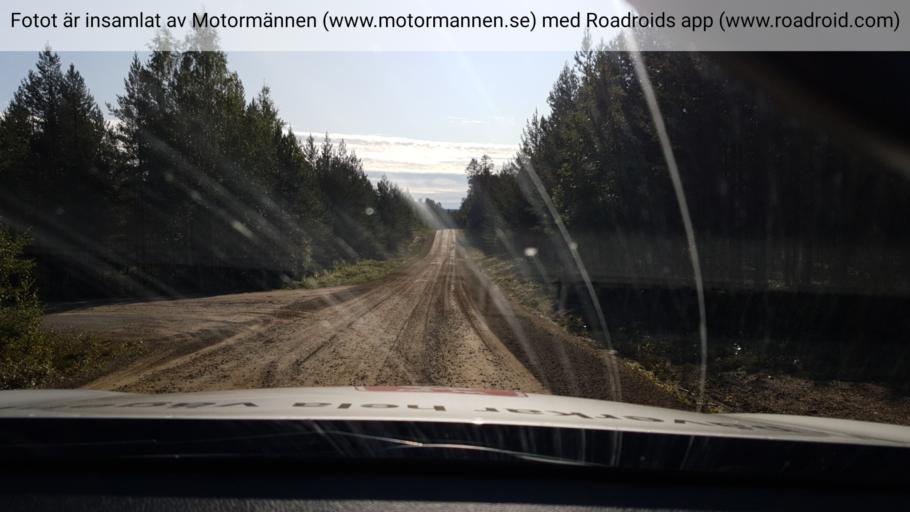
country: SE
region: Vaesterbotten
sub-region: Norsjo Kommun
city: Norsjoe
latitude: 64.6033
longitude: 19.3871
